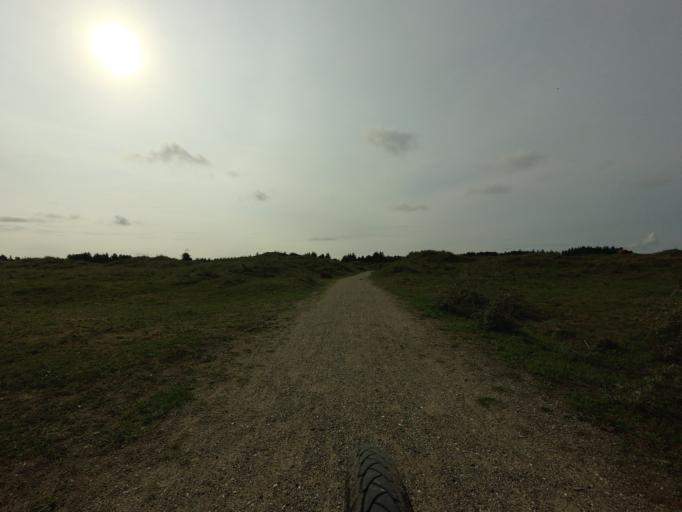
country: DK
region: North Denmark
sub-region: Hjorring Kommune
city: Sindal
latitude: 57.5898
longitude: 10.1477
